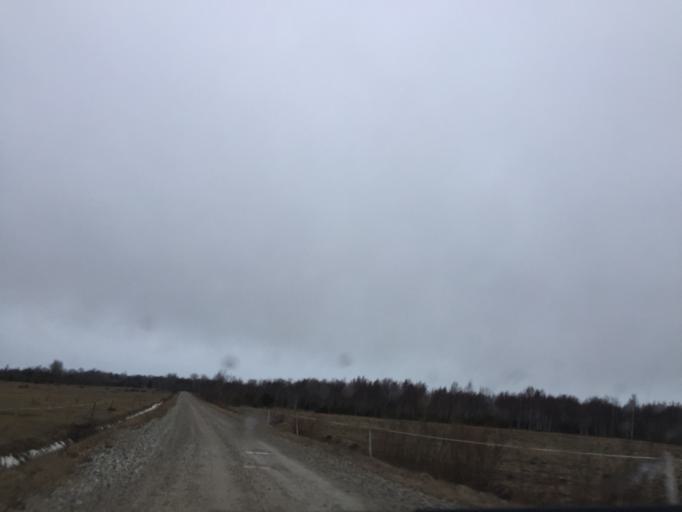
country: EE
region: Laeaene
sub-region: Haapsalu linn
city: Haapsalu
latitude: 58.6785
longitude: 23.5408
